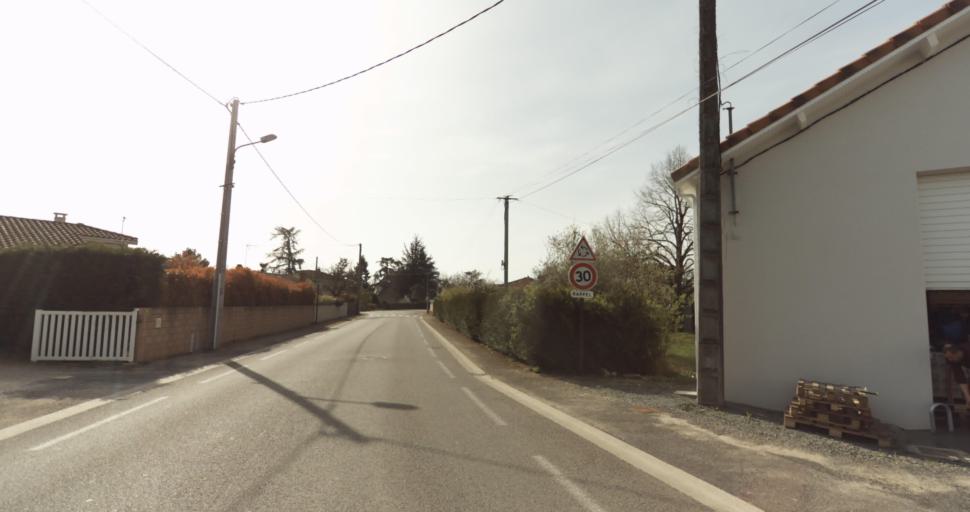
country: FR
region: Midi-Pyrenees
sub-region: Departement du Tarn
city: Saint-Sulpice-la-Pointe
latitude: 43.7807
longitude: 1.6809
